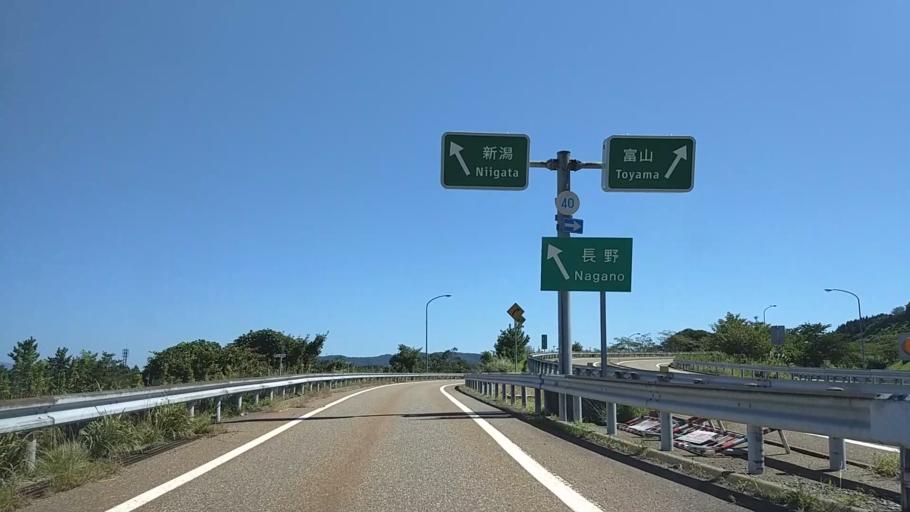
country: JP
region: Niigata
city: Joetsu
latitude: 37.1685
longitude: 138.1122
